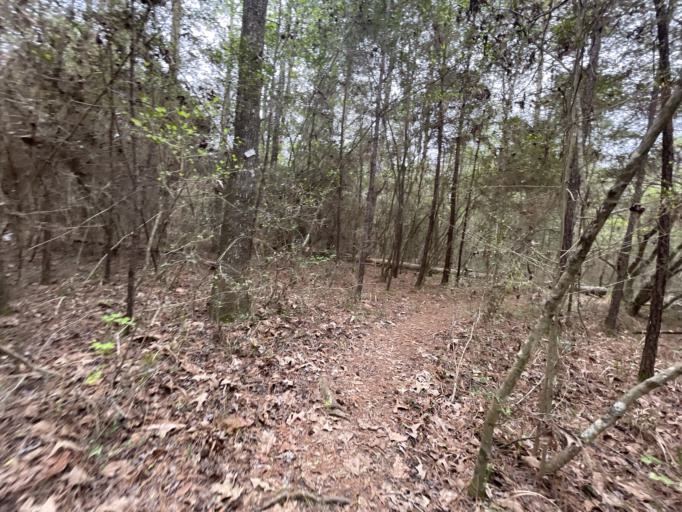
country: US
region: Texas
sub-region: Walker County
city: Huntsville
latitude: 30.6613
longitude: -95.4933
